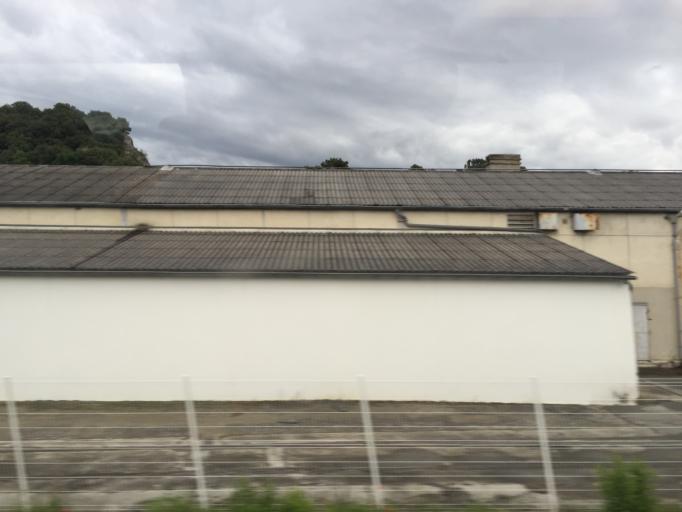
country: FR
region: Rhone-Alpes
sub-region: Departement de la Drome
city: Ancone
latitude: 44.5963
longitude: 4.7509
